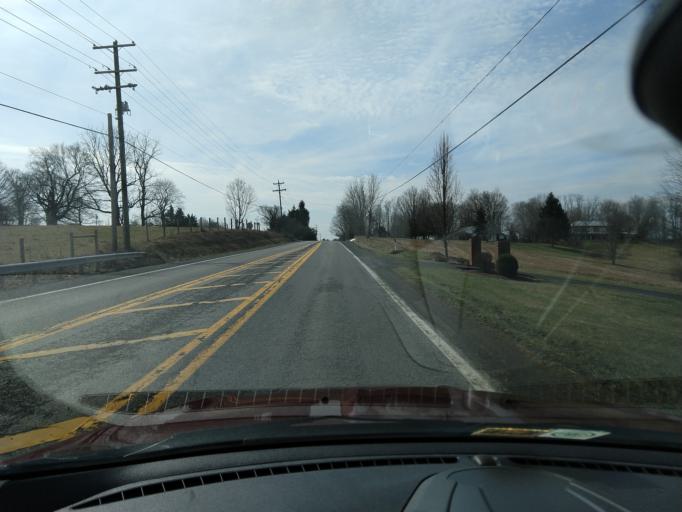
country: US
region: West Virginia
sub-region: Greenbrier County
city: Lewisburg
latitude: 37.8540
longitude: -80.4127
